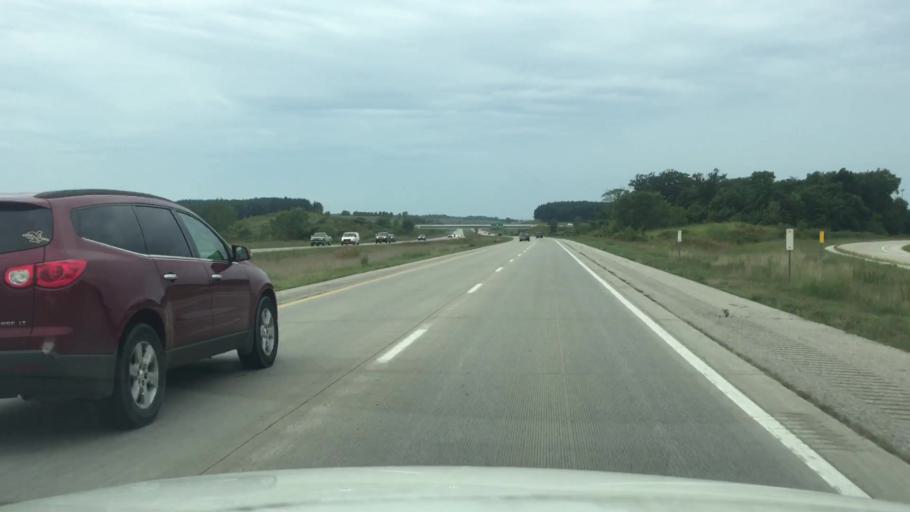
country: US
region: Iowa
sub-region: Polk County
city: West Des Moines
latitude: 41.5228
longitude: -93.7413
